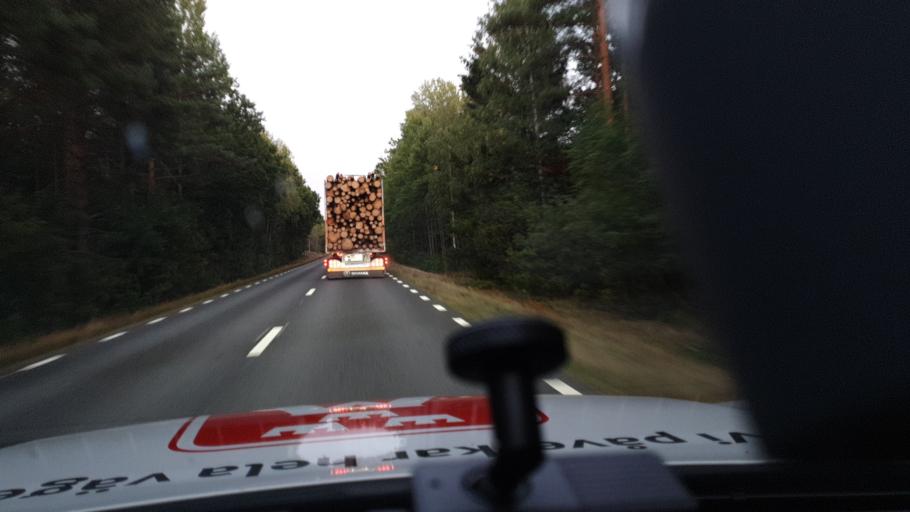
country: SE
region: Kalmar
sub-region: Hogsby Kommun
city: Hoegsby
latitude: 57.1200
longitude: 16.1944
